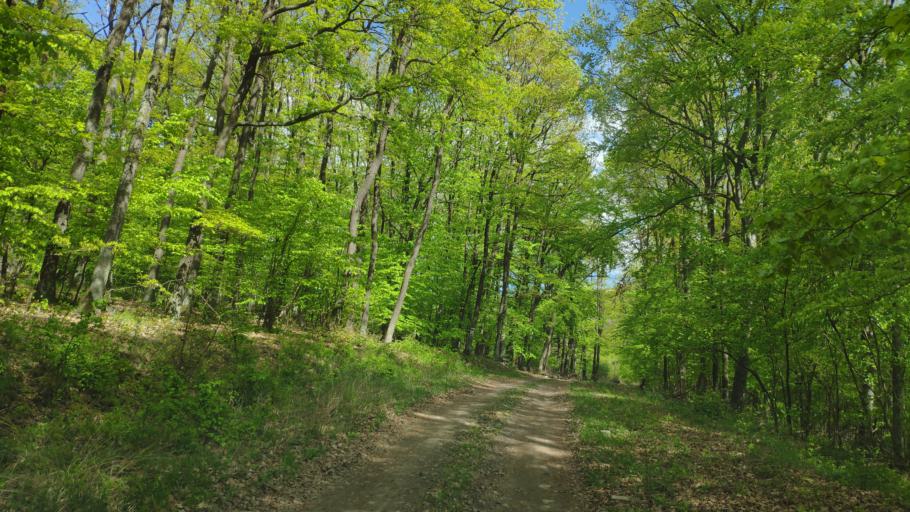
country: SK
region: Kosicky
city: Kosice
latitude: 48.6594
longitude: 21.4412
